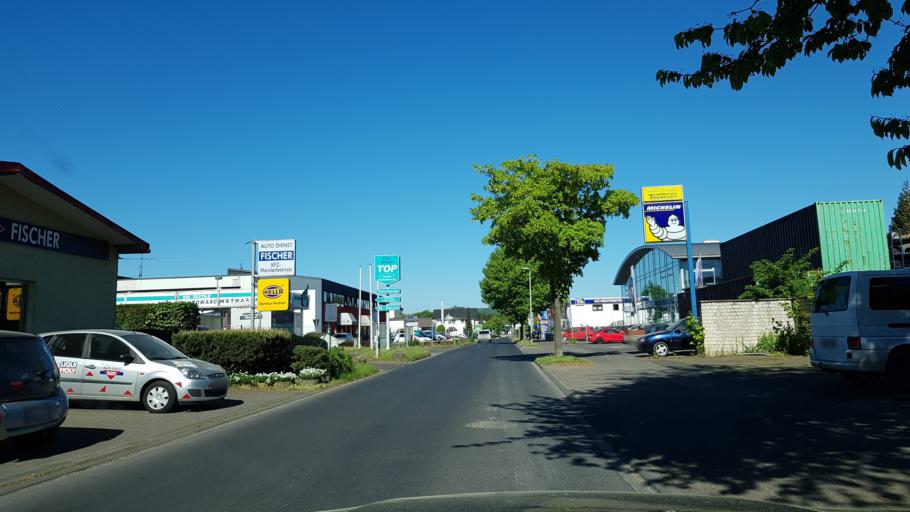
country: DE
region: North Rhine-Westphalia
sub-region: Regierungsbezirk Koln
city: Eitorf
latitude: 50.7710
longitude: 7.4681
